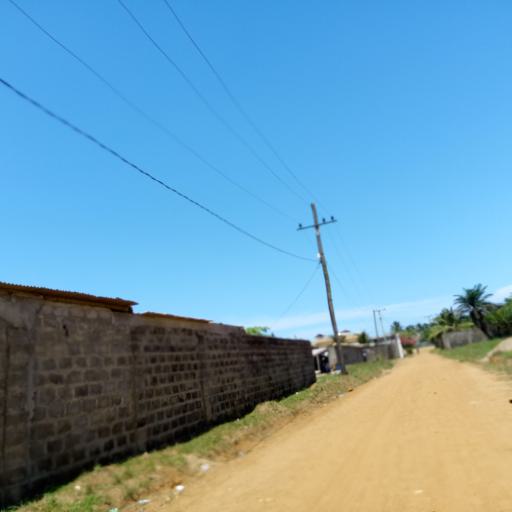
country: LR
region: Montserrado
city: Monrovia
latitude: 6.2342
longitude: -10.6922
